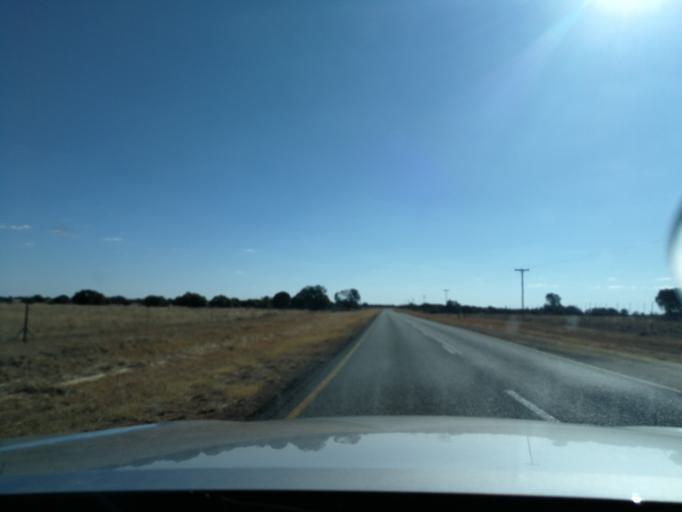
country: ZA
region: North-West
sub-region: Ngaka Modiri Molema District Municipality
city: Zeerust
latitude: -25.7798
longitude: 26.0037
